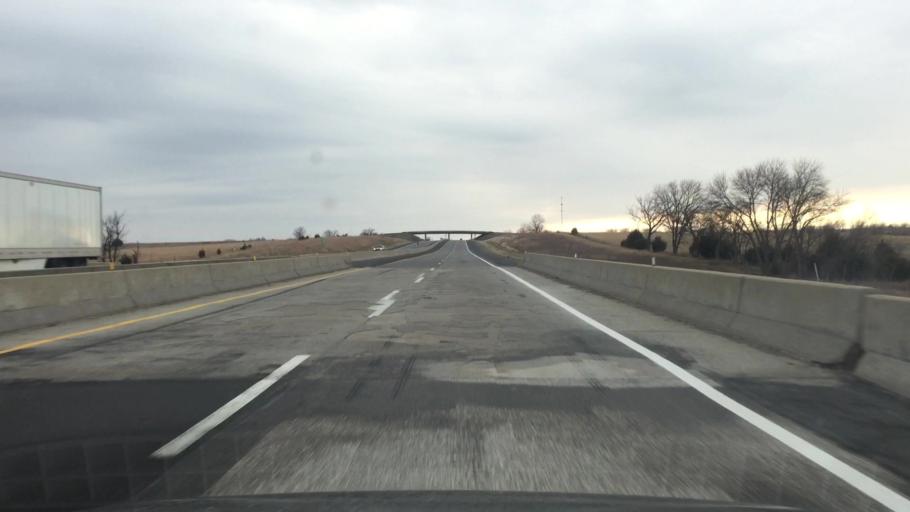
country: US
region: Kansas
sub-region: Osage County
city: Osage City
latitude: 38.7511
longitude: -95.9416
